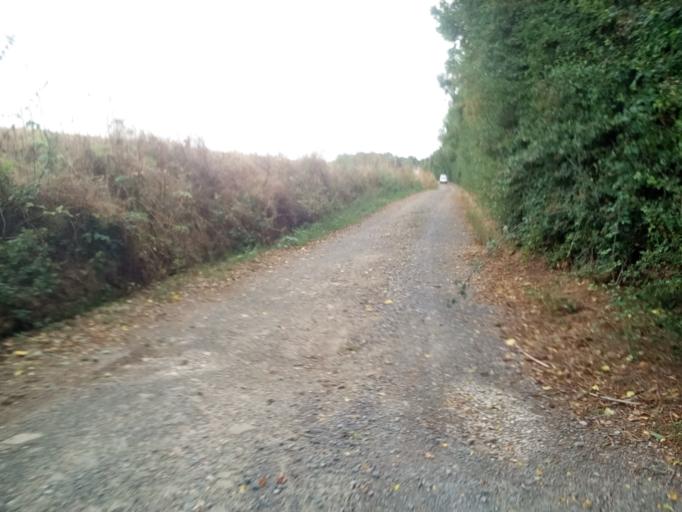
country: FR
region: Lower Normandy
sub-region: Departement du Calvados
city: Clinchamps-sur-Orne
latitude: 49.0637
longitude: -0.4178
